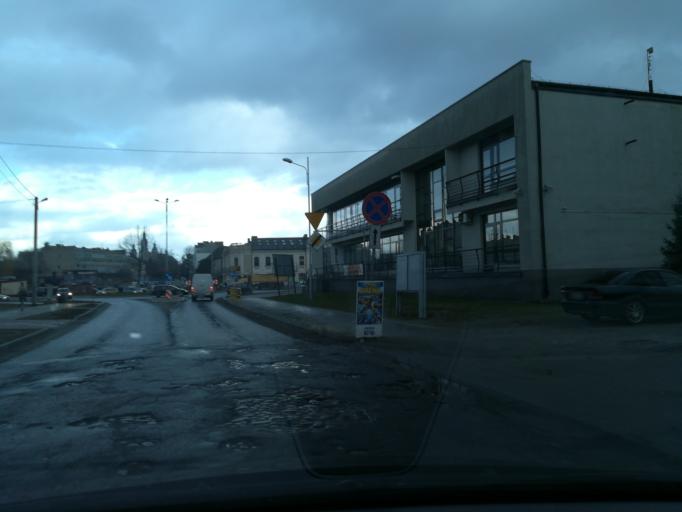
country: PL
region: Lodz Voivodeship
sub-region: Powiat radomszczanski
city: Radomsko
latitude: 51.0649
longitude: 19.4415
